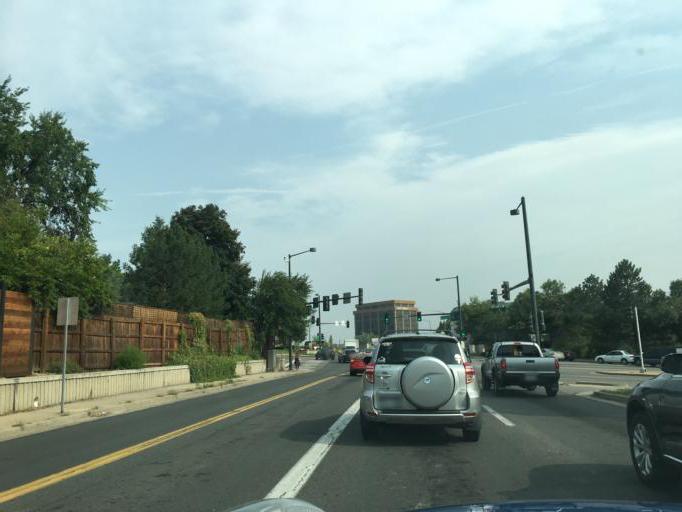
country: US
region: Colorado
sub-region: Arapahoe County
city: Glendale
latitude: 39.7118
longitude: -104.9371
